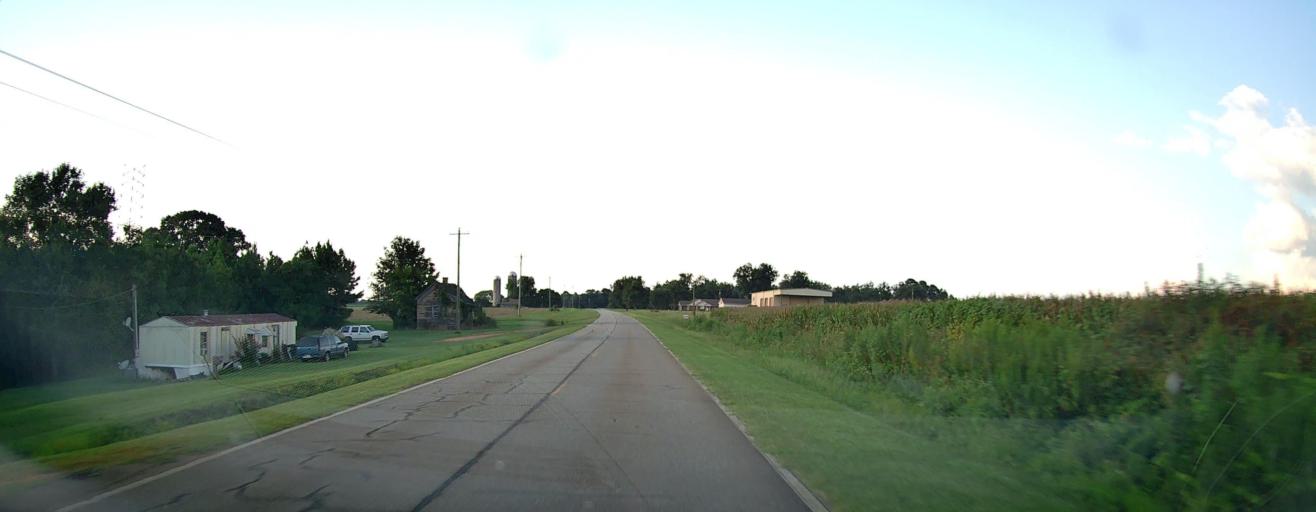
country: US
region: Georgia
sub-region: Peach County
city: Fort Valley
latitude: 32.6059
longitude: -83.8344
